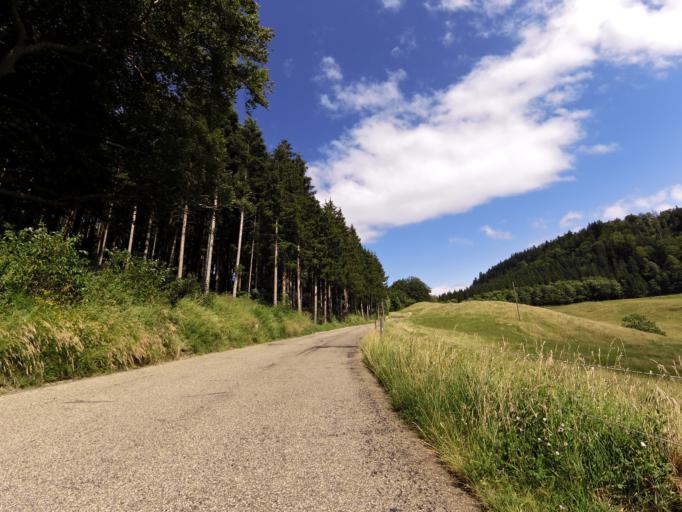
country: CH
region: Basel-Landschaft
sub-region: Bezirk Waldenburg
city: Langenbruck
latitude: 47.3657
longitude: 7.8000
